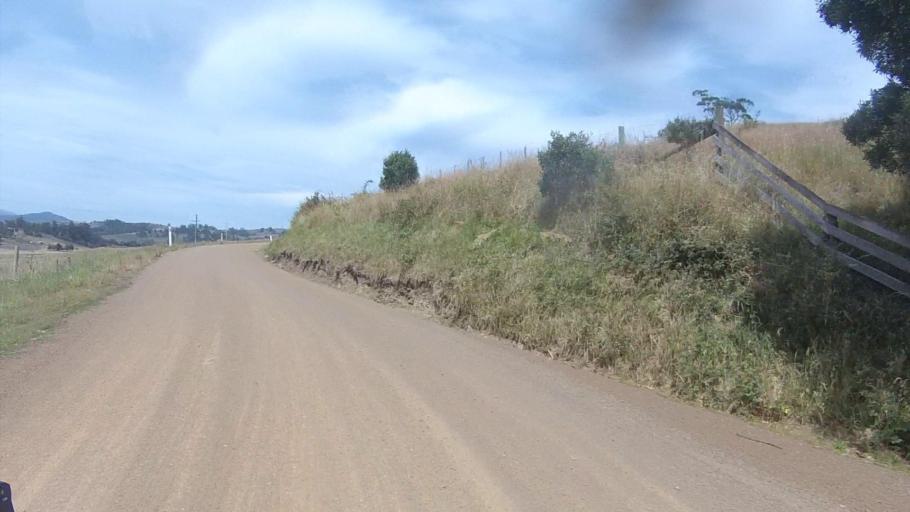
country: AU
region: Tasmania
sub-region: Sorell
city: Sorell
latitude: -42.7949
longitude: 147.8387
